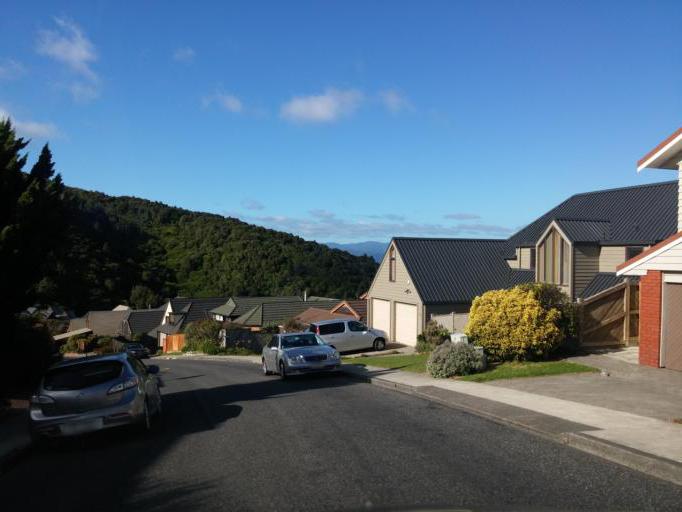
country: NZ
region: Wellington
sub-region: Wellington City
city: Kelburn
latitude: -41.2433
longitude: 174.7783
